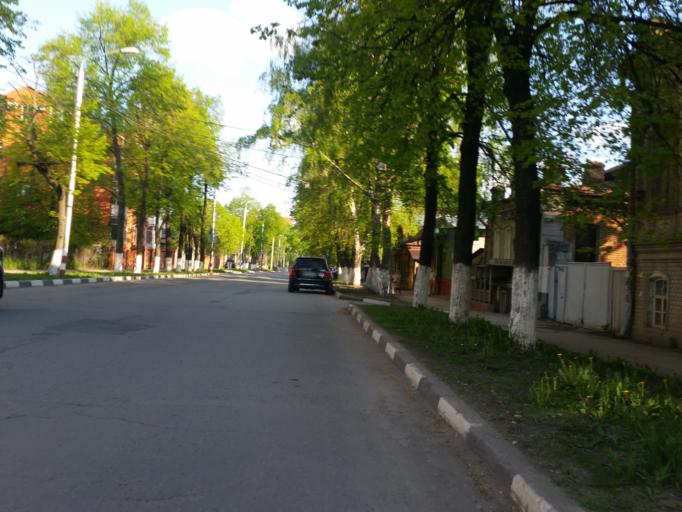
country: RU
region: Ulyanovsk
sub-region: Ulyanovskiy Rayon
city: Ulyanovsk
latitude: 54.3274
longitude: 48.3984
